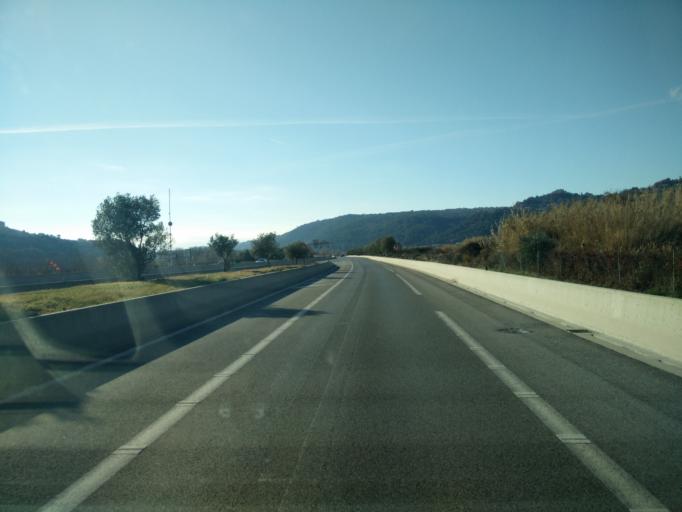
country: FR
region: Provence-Alpes-Cote d'Azur
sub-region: Departement des Alpes-Maritimes
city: Gattieres
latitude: 43.7582
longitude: 7.1931
